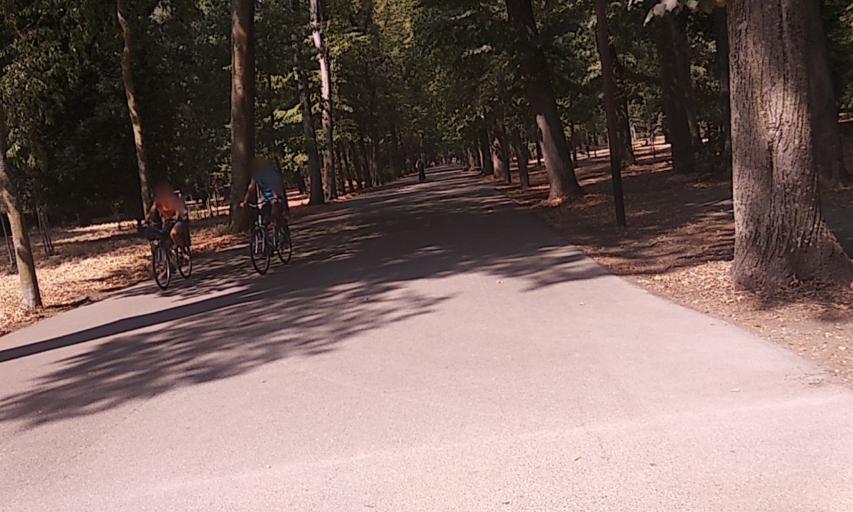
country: IT
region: Tuscany
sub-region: Province of Florence
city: Florence
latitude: 43.7779
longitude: 11.2286
